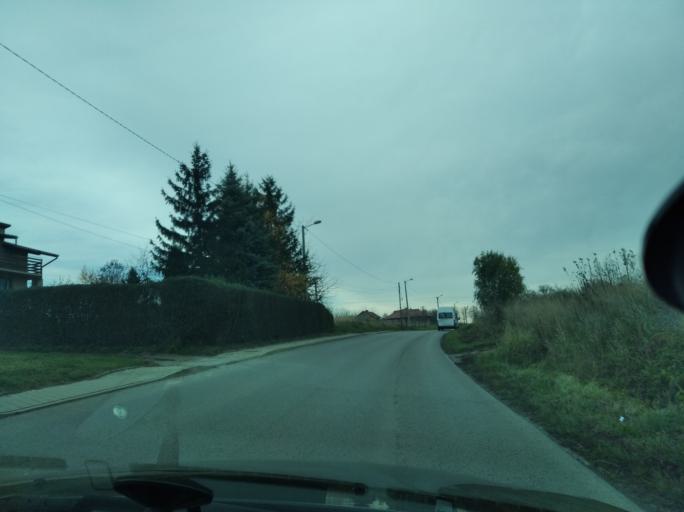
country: PL
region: Subcarpathian Voivodeship
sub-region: Powiat lancucki
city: Albigowa
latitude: 50.0322
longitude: 22.2376
